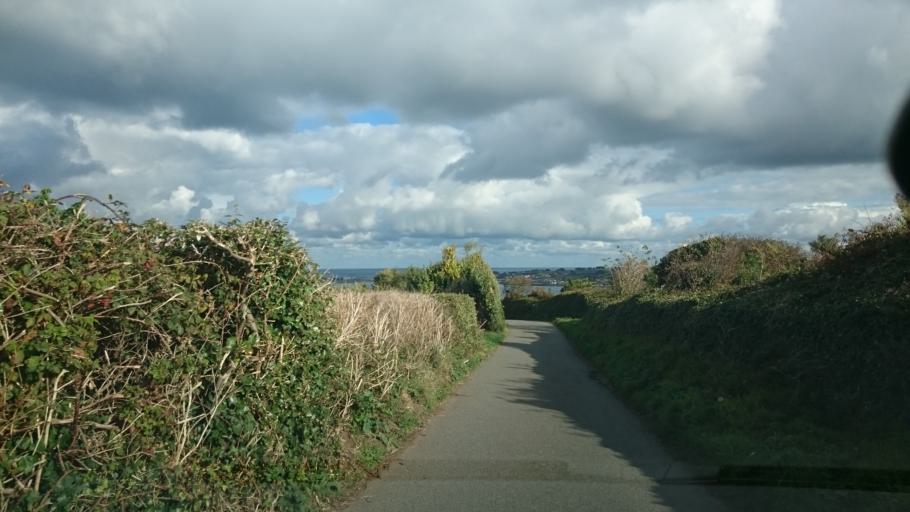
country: GG
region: St Peter Port
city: Saint Peter Port
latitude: 49.4318
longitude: -2.6657
